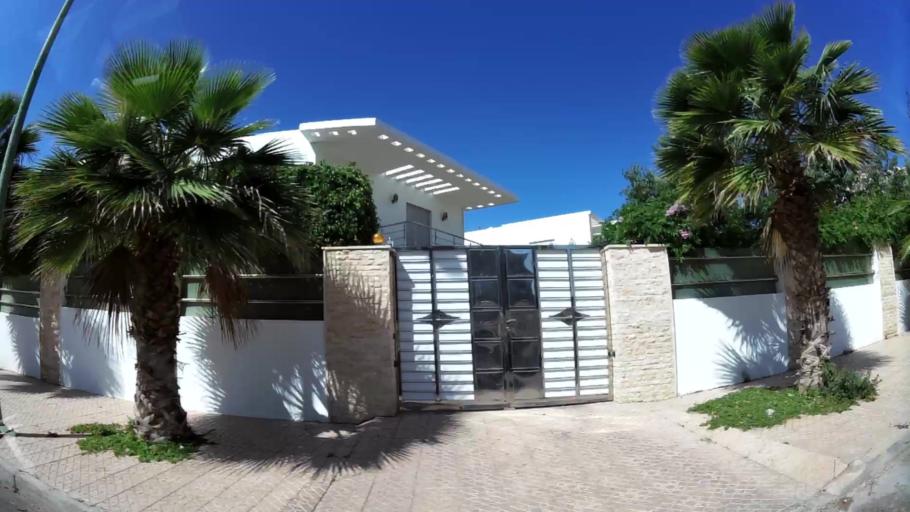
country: MA
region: Souss-Massa-Draa
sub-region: Agadir-Ida-ou-Tnan
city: Agadir
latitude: 30.4425
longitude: -9.5806
